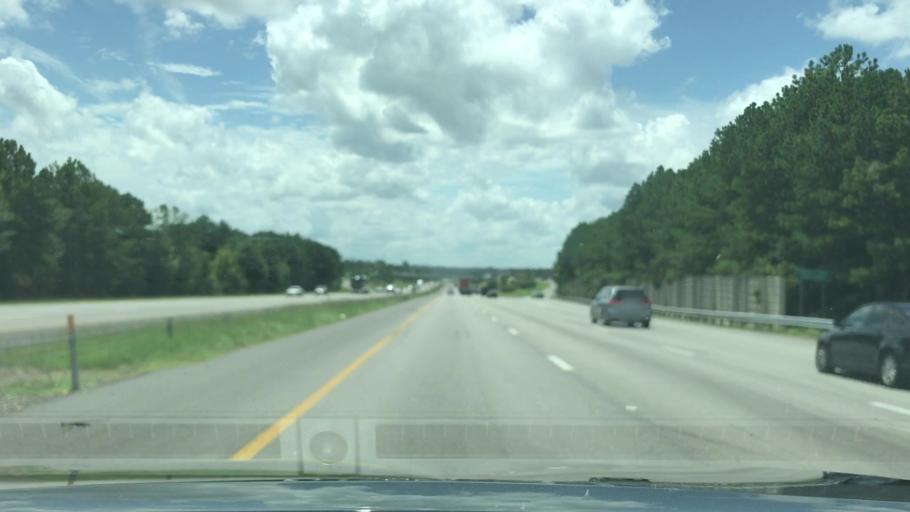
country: US
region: South Carolina
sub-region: Richland County
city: Woodfield
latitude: 34.0270
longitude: -80.9410
